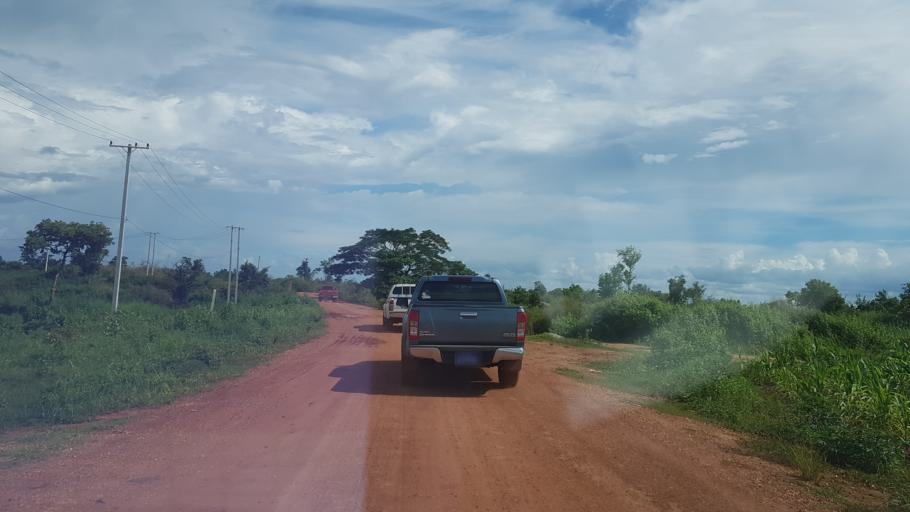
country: LA
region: Vientiane
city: Vientiane
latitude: 18.2100
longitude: 102.5659
